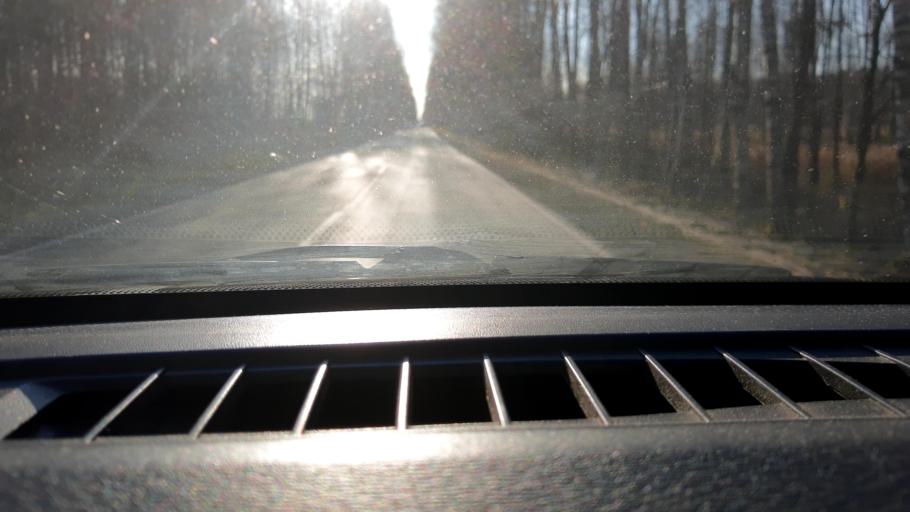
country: RU
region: Nizjnij Novgorod
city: Neklyudovo
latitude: 56.4895
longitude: 43.8620
